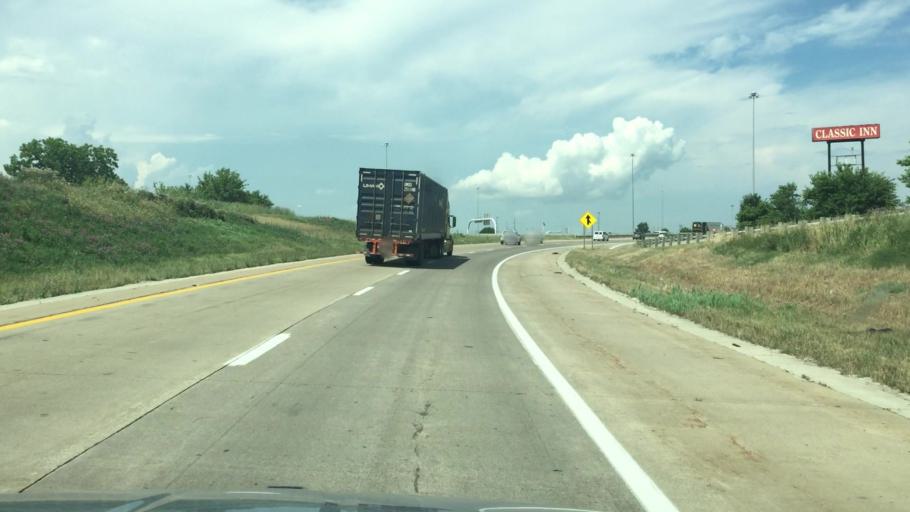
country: US
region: Ohio
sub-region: Lucas County
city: Toledo
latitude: 41.6883
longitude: -83.5151
